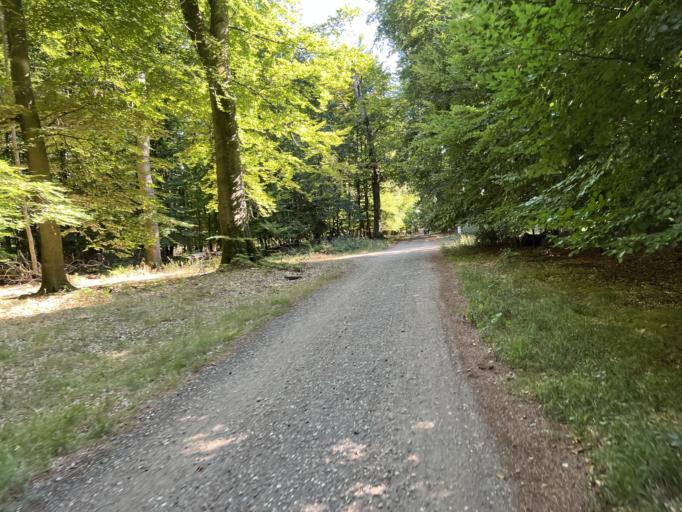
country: DE
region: Hesse
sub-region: Regierungsbezirk Darmstadt
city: Neu Isenburg
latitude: 50.0734
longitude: 8.6985
